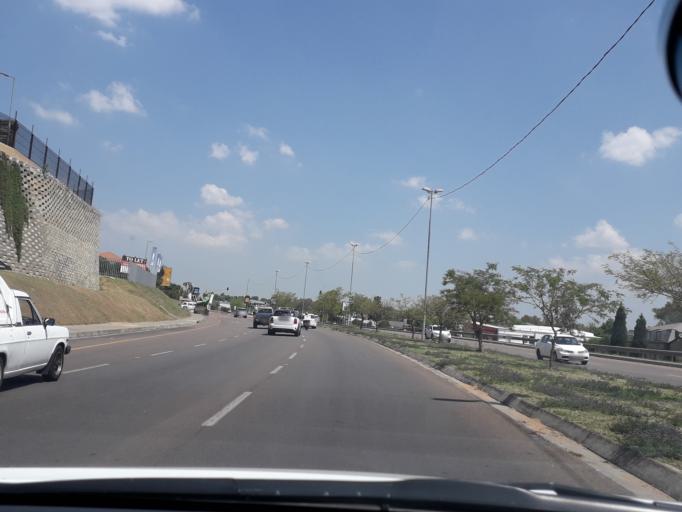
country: ZA
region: Gauteng
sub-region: City of Johannesburg Metropolitan Municipality
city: Midrand
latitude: -26.0316
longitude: 28.0608
